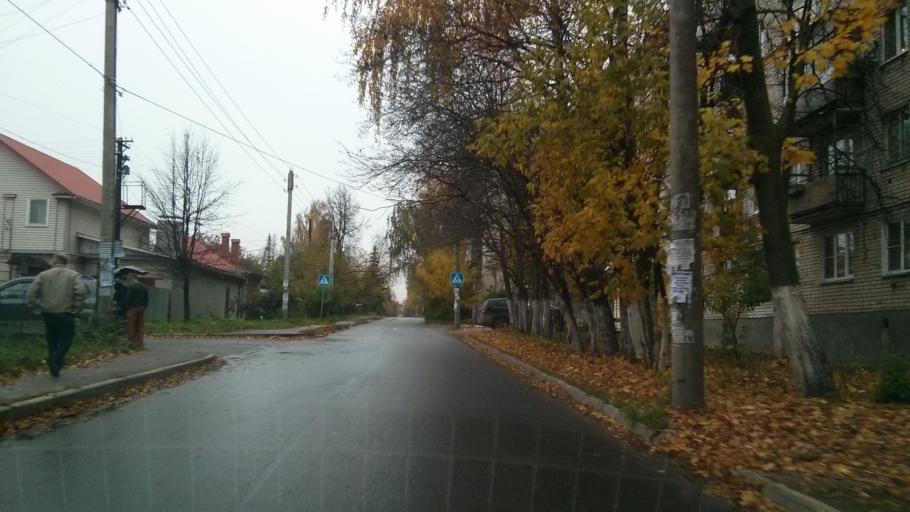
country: RU
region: Nizjnij Novgorod
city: Nizhniy Novgorod
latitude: 56.2930
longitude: 44.0287
